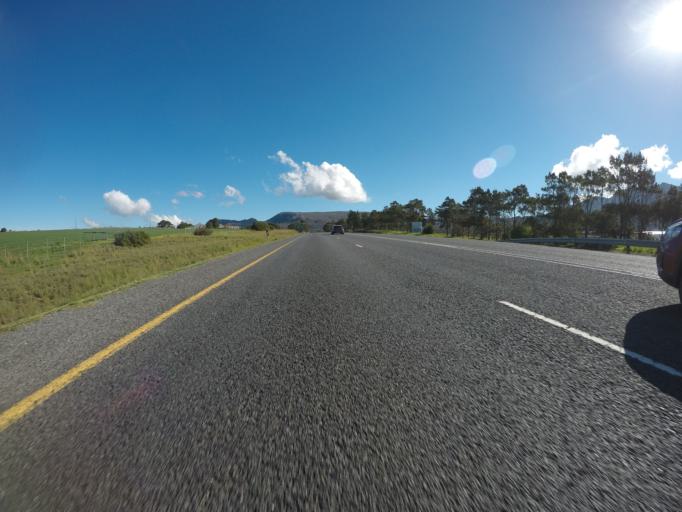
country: ZA
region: Western Cape
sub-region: Overberg District Municipality
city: Hermanus
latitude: -34.2356
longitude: 19.2105
